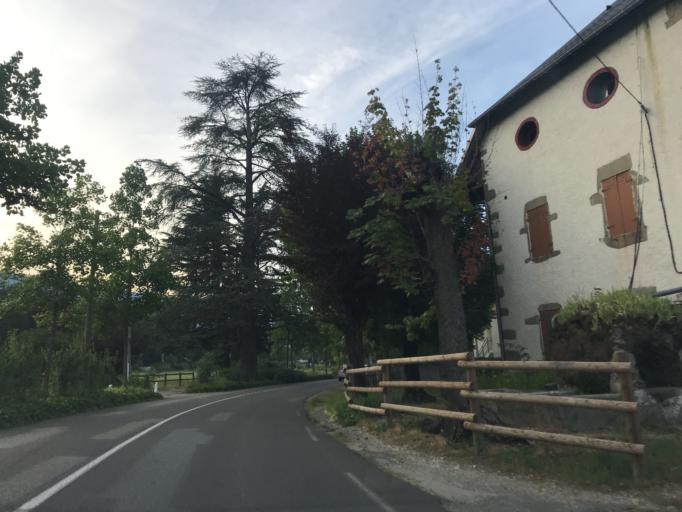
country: FR
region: Rhone-Alpes
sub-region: Departement de la Savoie
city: Cognin
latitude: 45.5751
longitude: 5.8883
